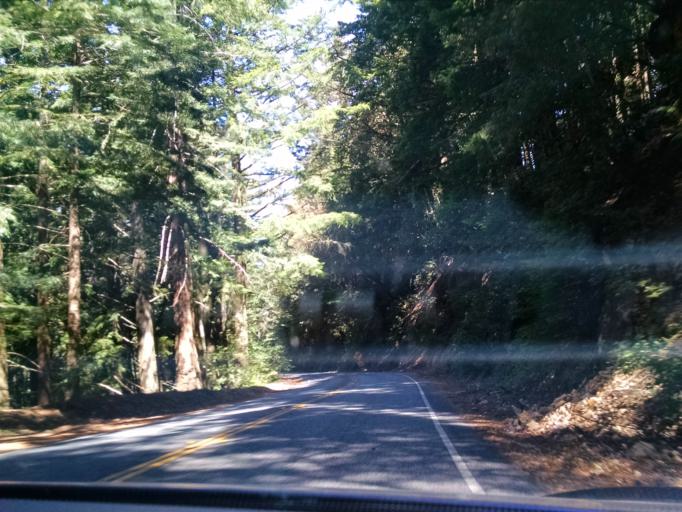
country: US
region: California
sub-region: San Mateo County
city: Woodside
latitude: 37.4209
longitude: -122.3189
